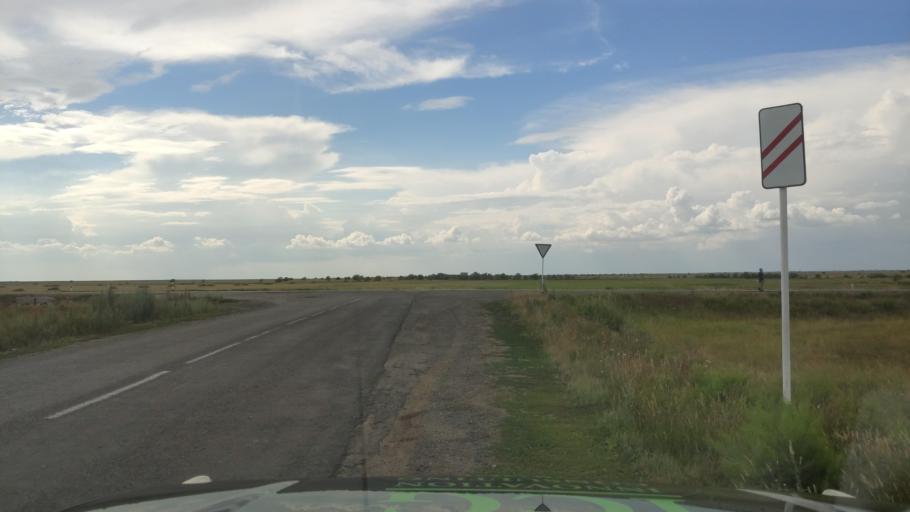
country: KZ
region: Pavlodar
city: Pavlodar
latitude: 52.6613
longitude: 77.4926
